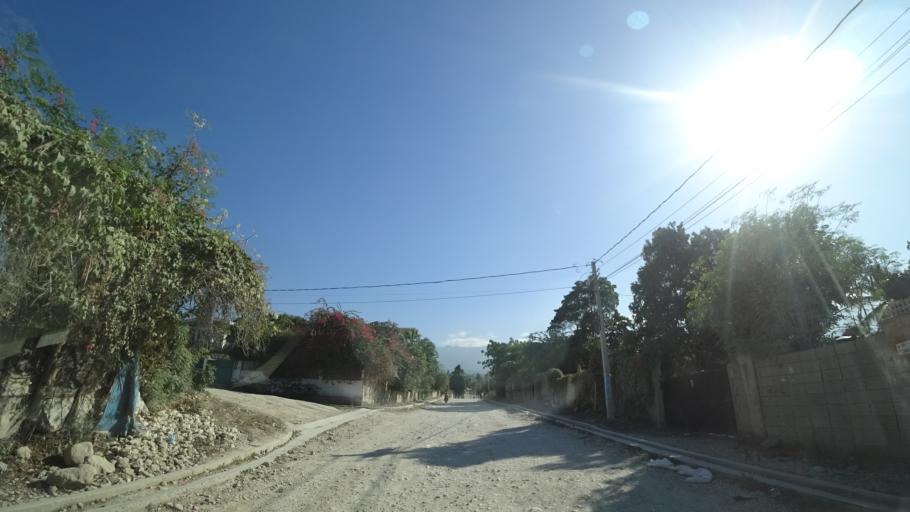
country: HT
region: Ouest
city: Delmas 73
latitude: 18.5473
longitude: -72.2870
